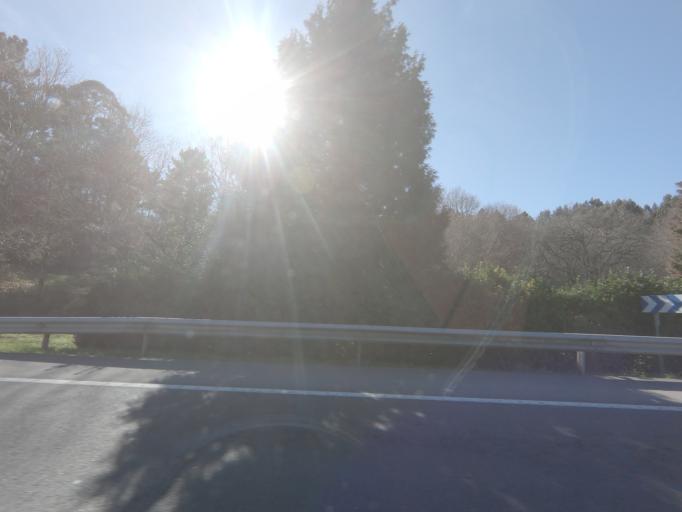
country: ES
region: Galicia
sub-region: Provincia de Pontevedra
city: Silleda
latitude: 42.6870
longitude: -8.2193
